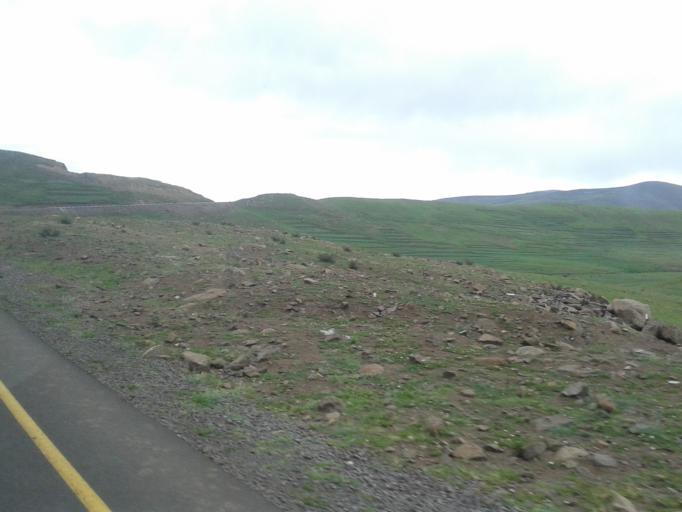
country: LS
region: Maseru
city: Nako
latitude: -29.7896
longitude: 28.0233
